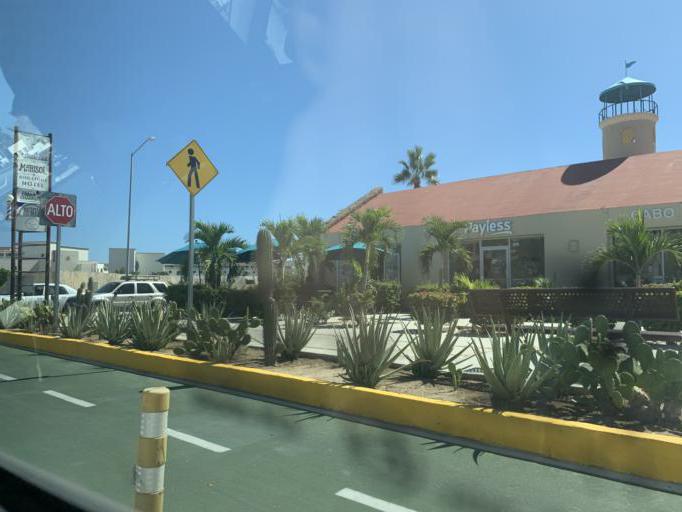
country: MX
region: Baja California Sur
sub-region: Los Cabos
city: San Jose del Cabo
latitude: 23.0411
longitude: -109.7052
